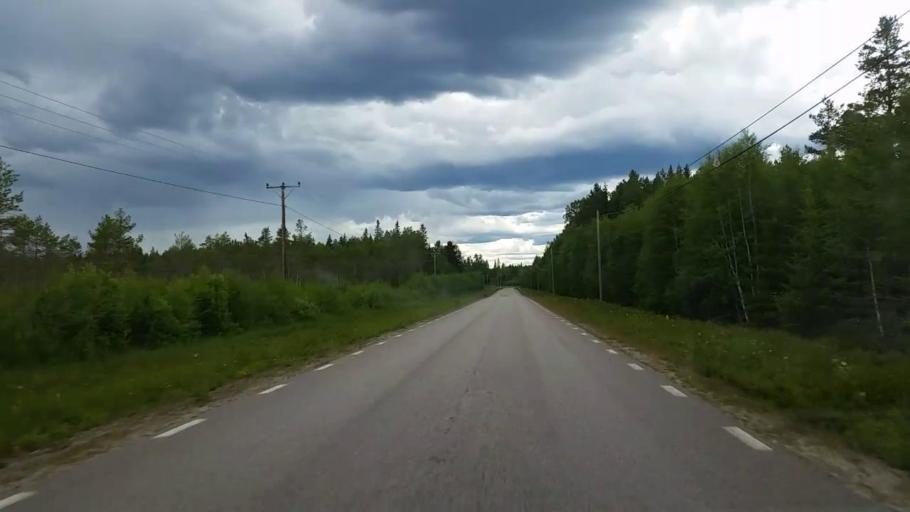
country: SE
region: Gaevleborg
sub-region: Ovanakers Kommun
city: Edsbyn
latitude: 61.4534
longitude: 15.8783
